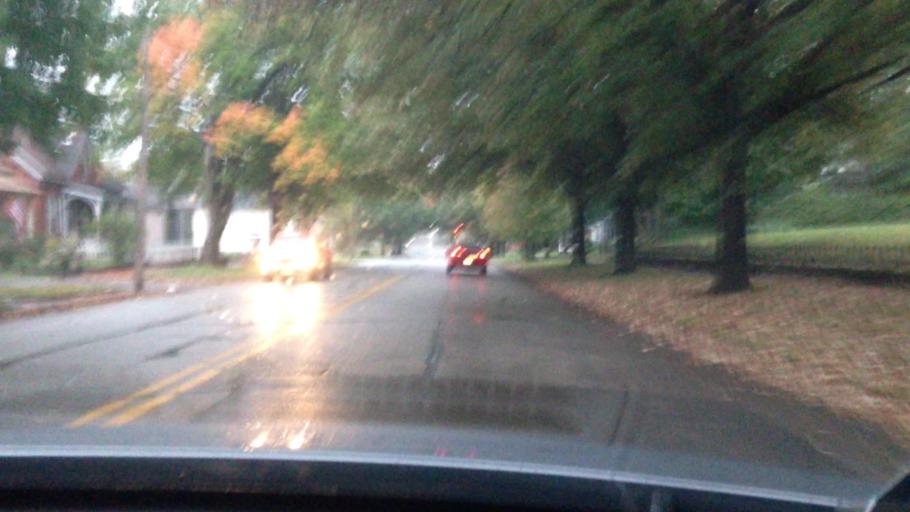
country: US
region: Kansas
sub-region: Leavenworth County
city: Leavenworth
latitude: 39.3122
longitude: -94.9208
